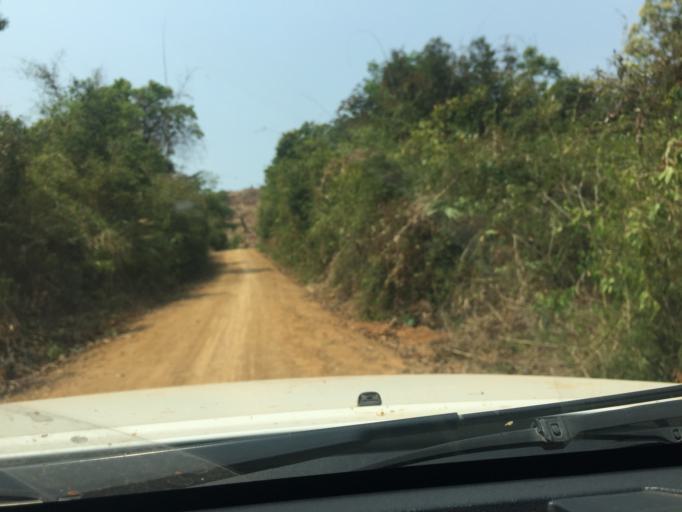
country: LA
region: Loungnamtha
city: Muang Nale
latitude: 20.6301
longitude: 101.6455
